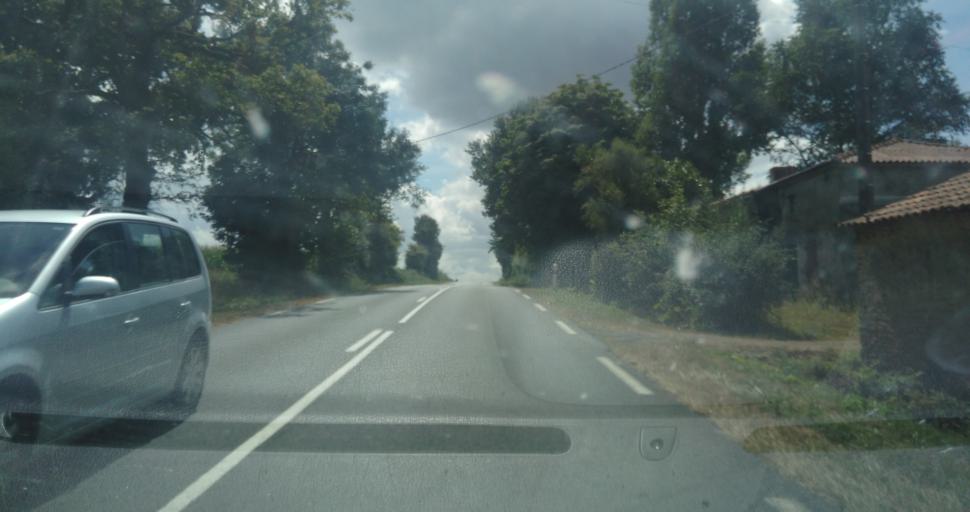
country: FR
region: Pays de la Loire
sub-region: Departement de la Vendee
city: Bournezeau
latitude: 46.6088
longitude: -1.1424
